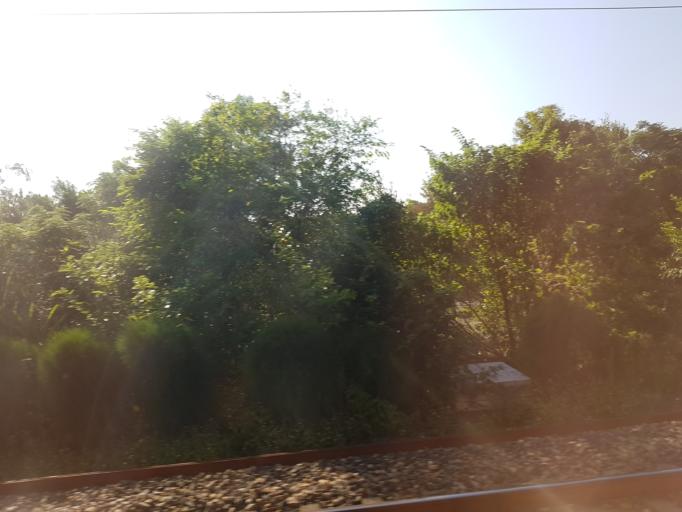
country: TW
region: Taiwan
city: Fengyuan
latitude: 24.2926
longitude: 120.7328
